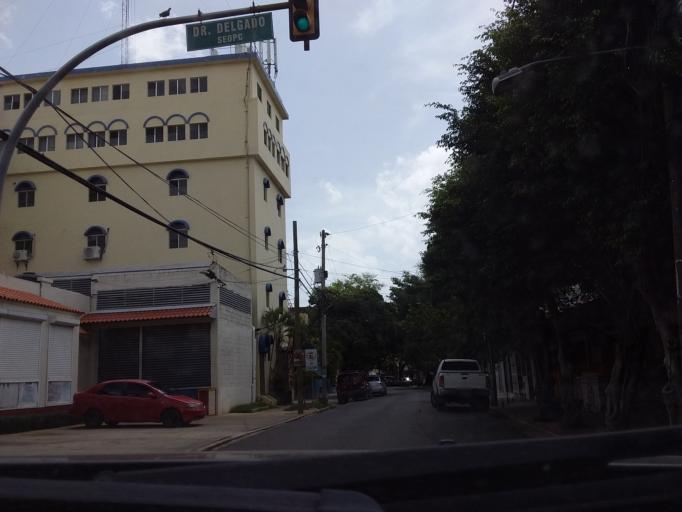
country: DO
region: Nacional
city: Ciudad Nueva
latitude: 18.4693
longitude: -69.8970
